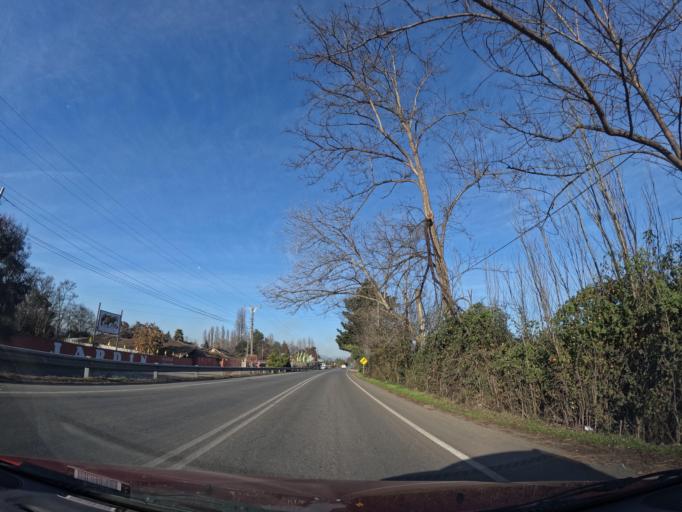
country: CL
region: Maule
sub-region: Provincia de Talca
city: San Clemente
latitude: -35.6231
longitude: -71.4855
